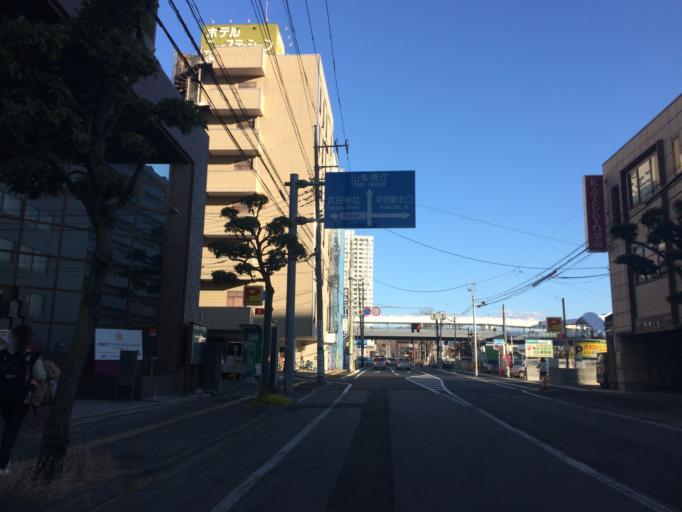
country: JP
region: Yamanashi
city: Kofu-shi
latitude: 35.6687
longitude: 138.5680
